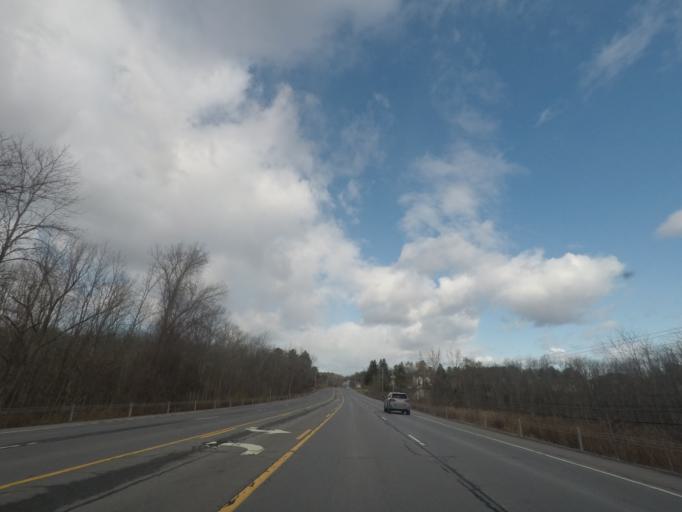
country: US
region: New York
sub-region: Saratoga County
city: Ballston Spa
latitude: 42.9997
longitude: -73.7908
